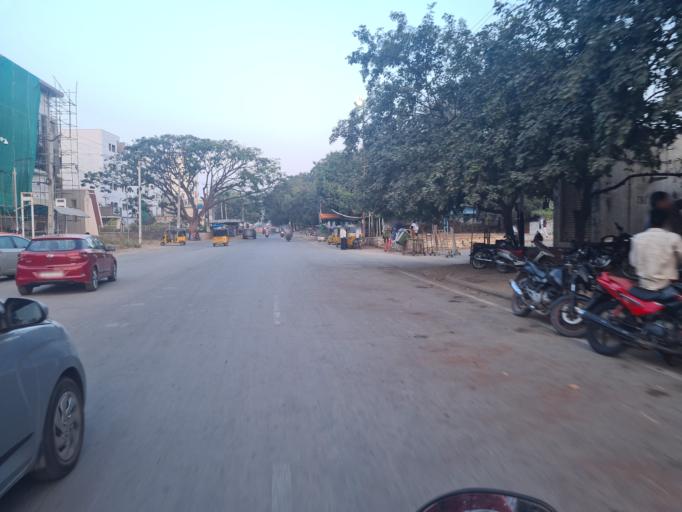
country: IN
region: Telangana
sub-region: Medak
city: Serilingampalle
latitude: 17.4836
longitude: 78.3163
